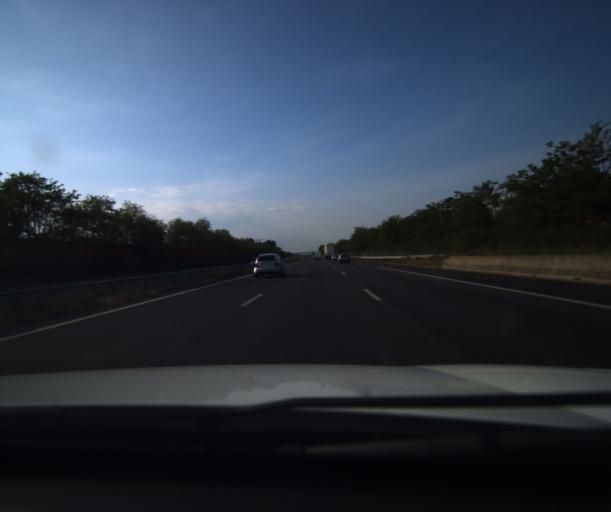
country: FR
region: Midi-Pyrenees
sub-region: Departement de la Haute-Garonne
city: Saint-Alban
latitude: 43.6991
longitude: 1.4078
